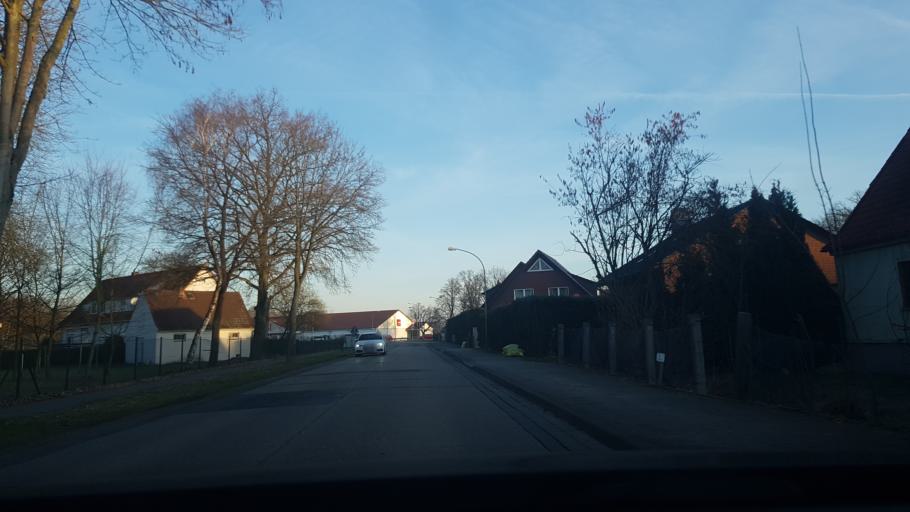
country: DE
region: Lower Saxony
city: Gifhorn
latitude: 52.5107
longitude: 10.5827
